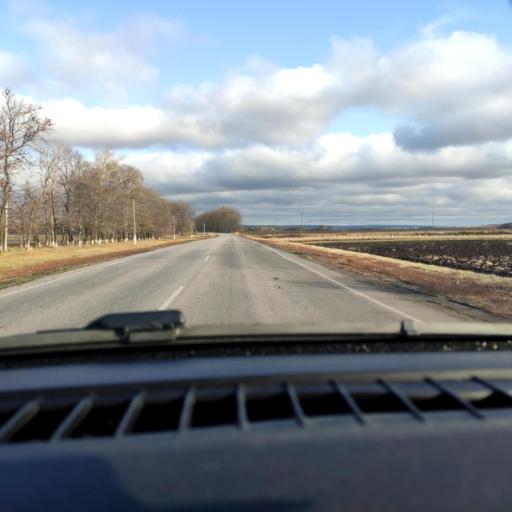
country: RU
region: Belgorod
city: Ilovka
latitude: 50.7377
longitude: 38.7050
